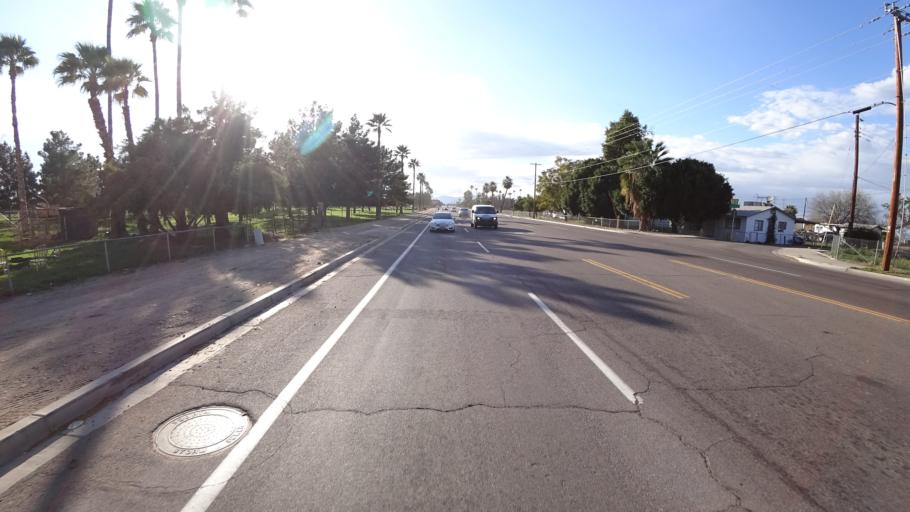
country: US
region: Arizona
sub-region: Maricopa County
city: Peoria
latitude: 33.5523
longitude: -112.2212
